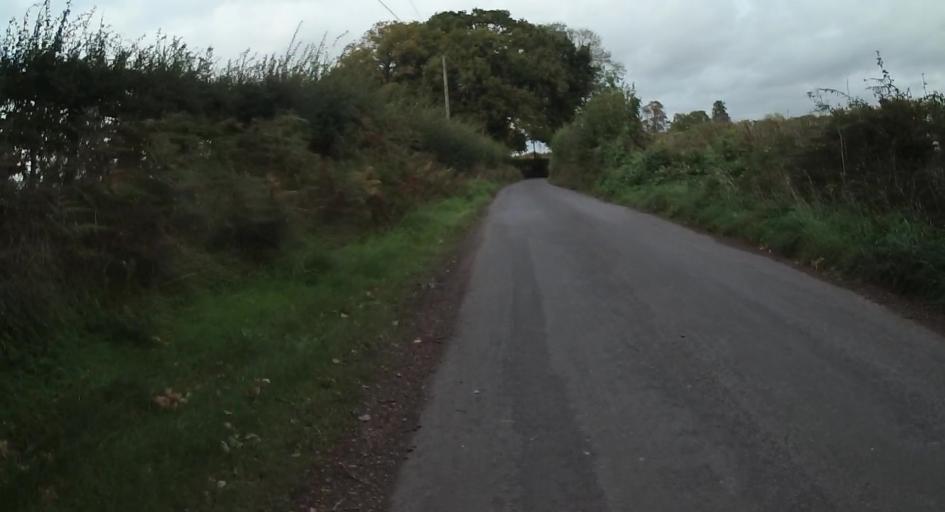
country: GB
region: England
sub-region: Hampshire
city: Kingsley
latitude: 51.1471
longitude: -0.9198
